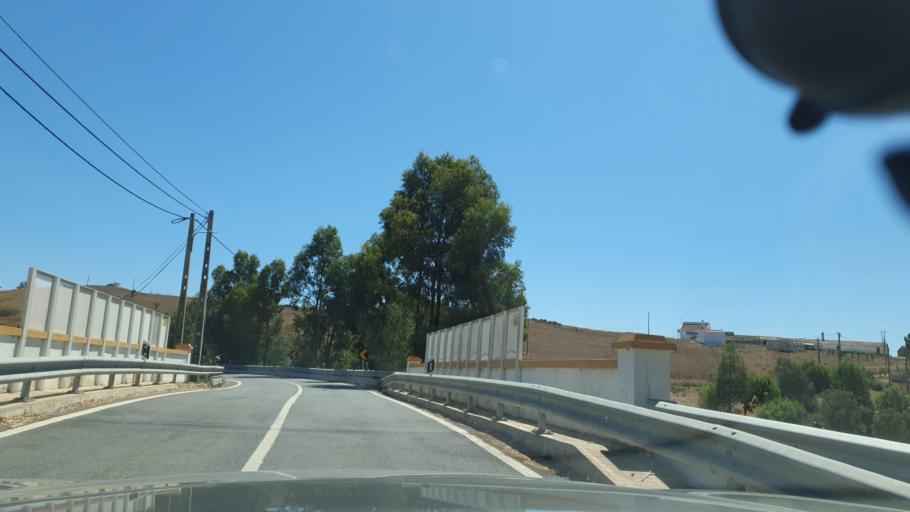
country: PT
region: Beja
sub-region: Odemira
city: Odemira
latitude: 37.4935
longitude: -8.4814
